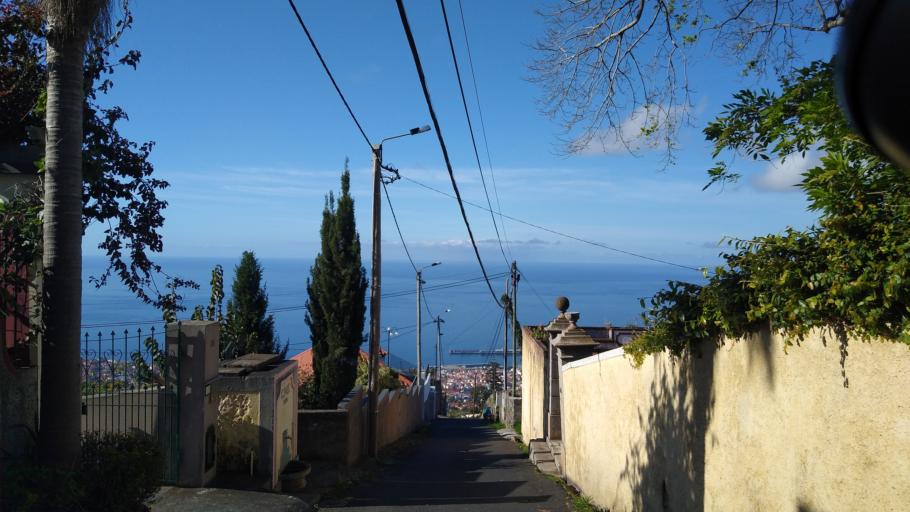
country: PT
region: Madeira
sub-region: Funchal
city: Nossa Senhora do Monte
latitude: 32.6718
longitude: -16.9022
